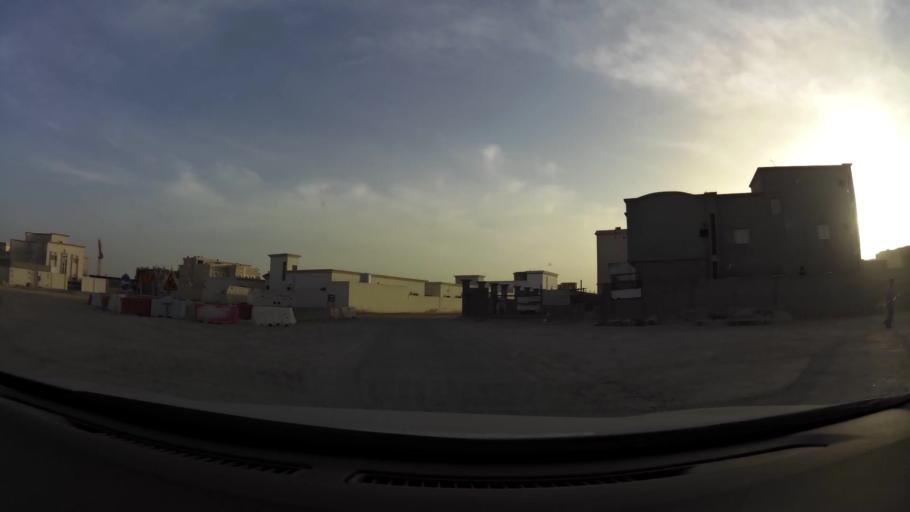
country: QA
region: Al Wakrah
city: Al Wakrah
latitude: 25.1435
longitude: 51.5954
